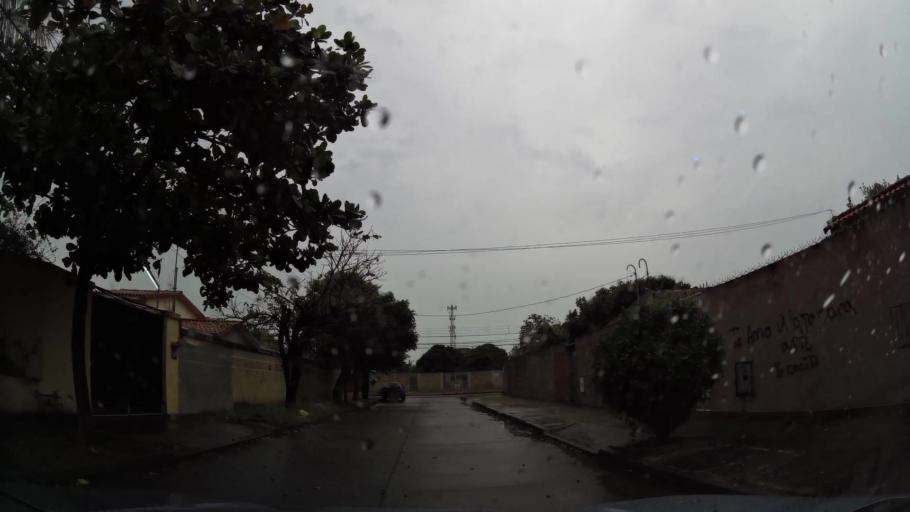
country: BO
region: Santa Cruz
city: Santa Cruz de la Sierra
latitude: -17.7704
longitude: -63.1485
